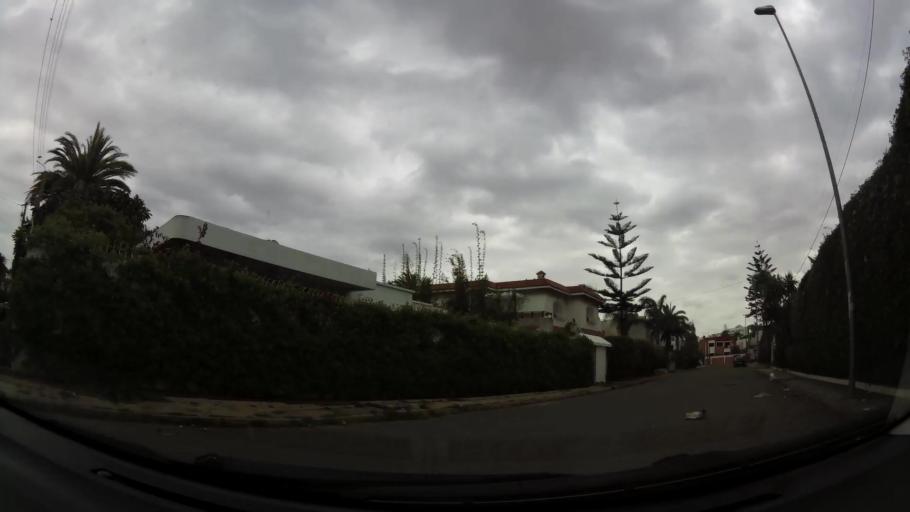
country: MA
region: Grand Casablanca
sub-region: Casablanca
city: Casablanca
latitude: 33.5709
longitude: -7.6588
